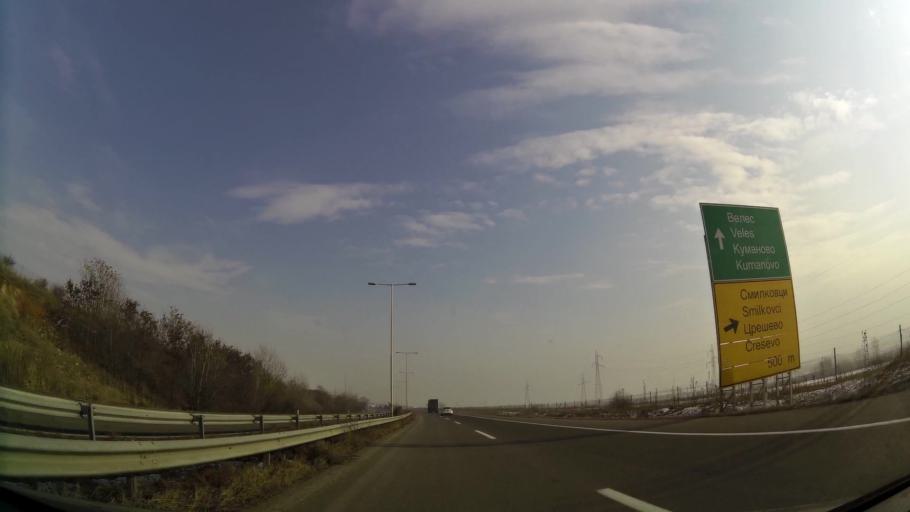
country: MK
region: Butel
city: Butel
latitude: 42.0326
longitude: 21.4773
